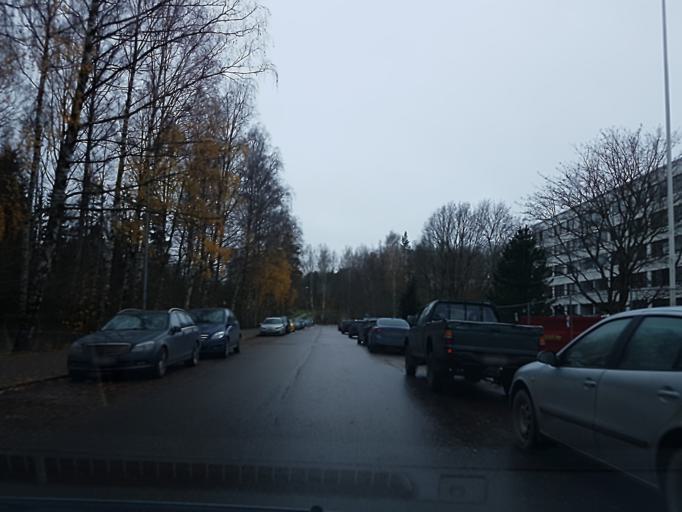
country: FI
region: Uusimaa
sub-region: Helsinki
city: Vantaa
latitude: 60.2319
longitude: 25.0877
